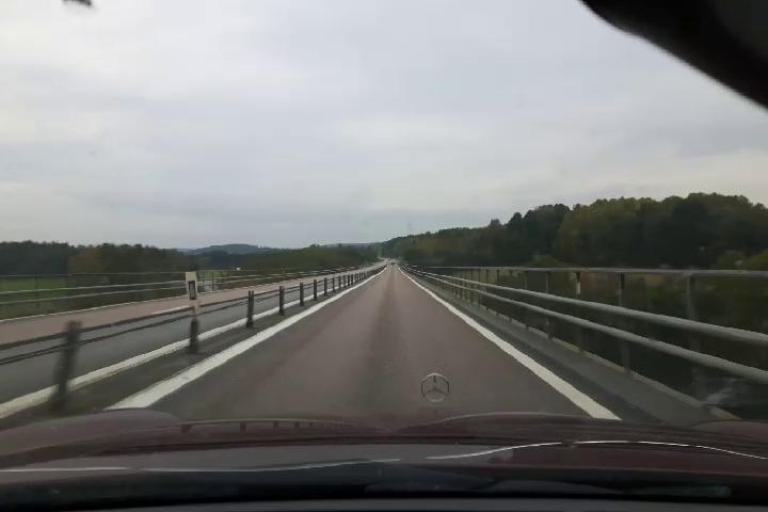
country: SE
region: Vaesternorrland
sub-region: Haernoesands Kommun
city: Haernoesand
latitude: 62.8571
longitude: 18.0194
